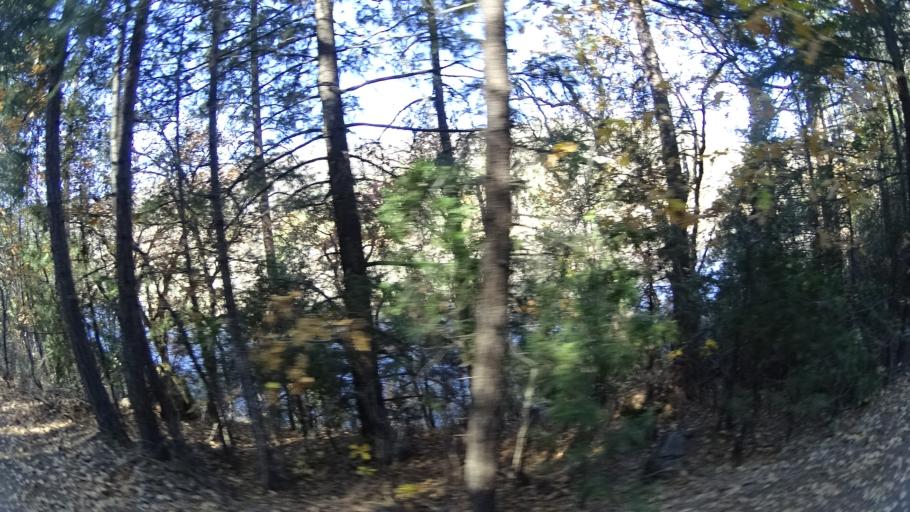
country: US
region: California
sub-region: Siskiyou County
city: Yreka
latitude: 41.8613
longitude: -122.8191
